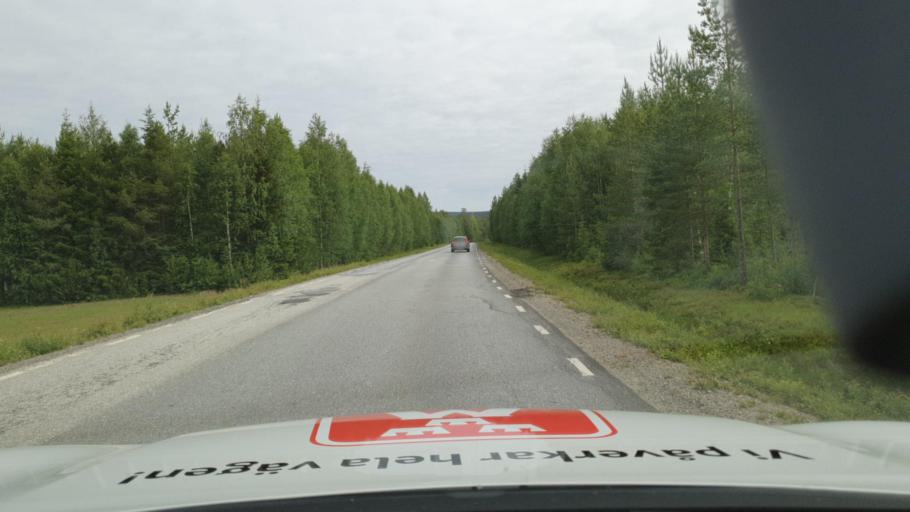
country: SE
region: Vaesterbotten
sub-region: Vindelns Kommun
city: Vindeln
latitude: 64.2213
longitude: 19.7646
